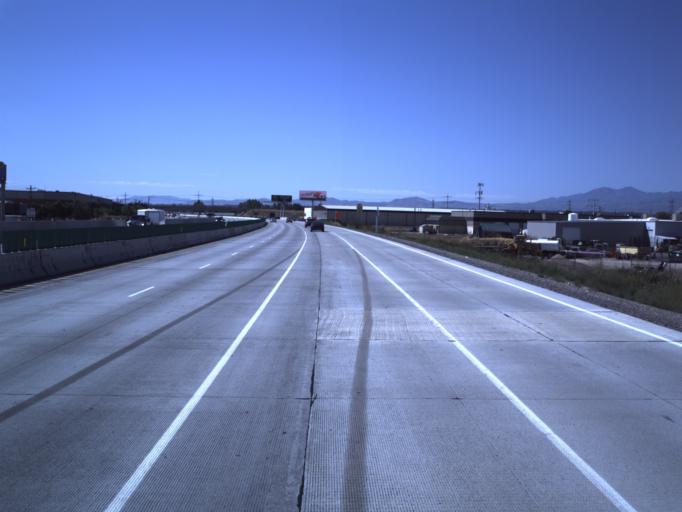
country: US
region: Utah
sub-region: Salt Lake County
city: Taylorsville
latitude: 40.7191
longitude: -111.9535
